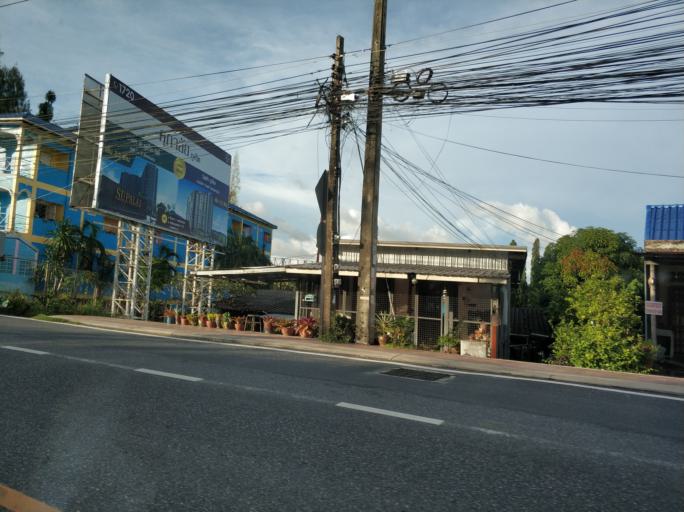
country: TH
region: Phuket
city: Kathu
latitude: 7.9019
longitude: 98.3399
